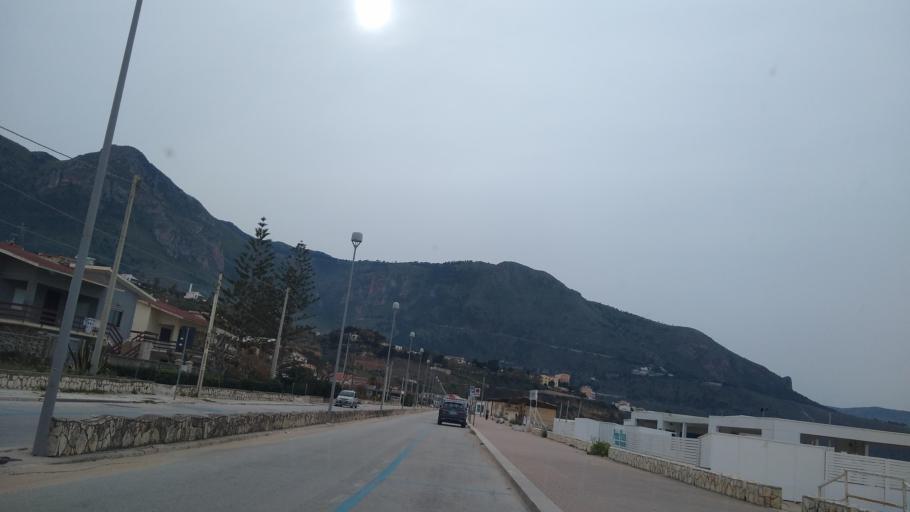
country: IT
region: Sicily
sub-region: Trapani
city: Castellammare del Golfo
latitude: 38.0239
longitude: 12.9006
